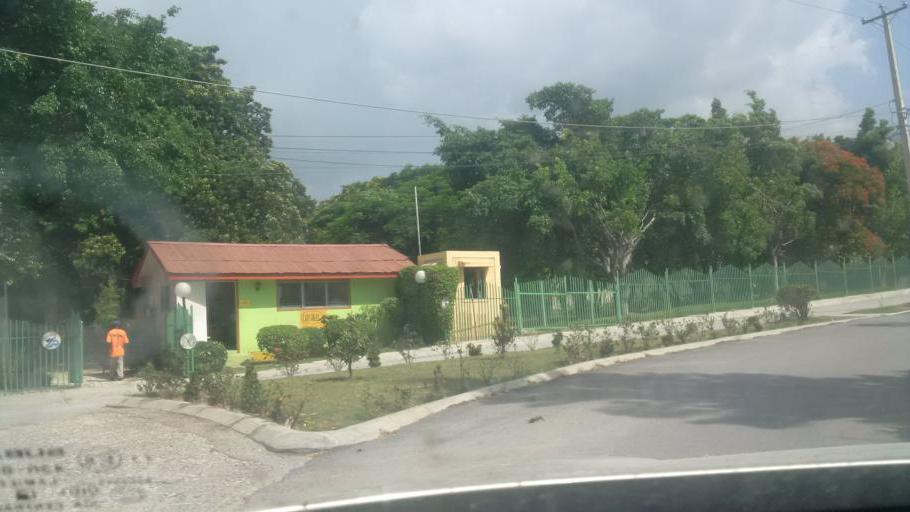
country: HT
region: Ouest
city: Petionville
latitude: 18.5253
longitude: -72.2547
